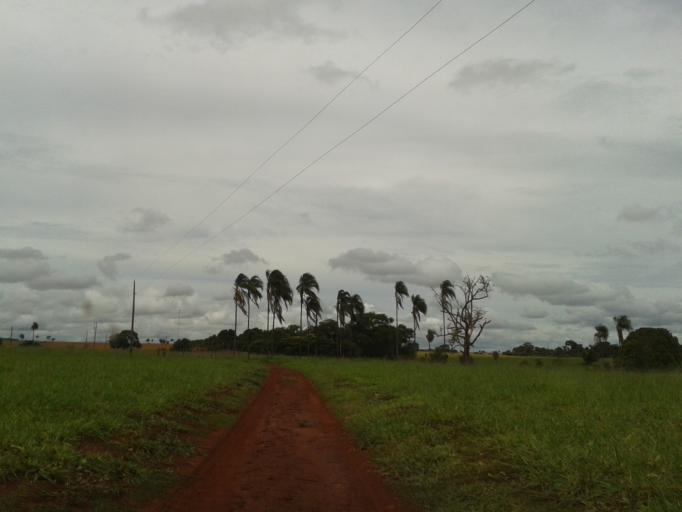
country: BR
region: Minas Gerais
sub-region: Capinopolis
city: Capinopolis
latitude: -18.7768
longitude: -49.7757
